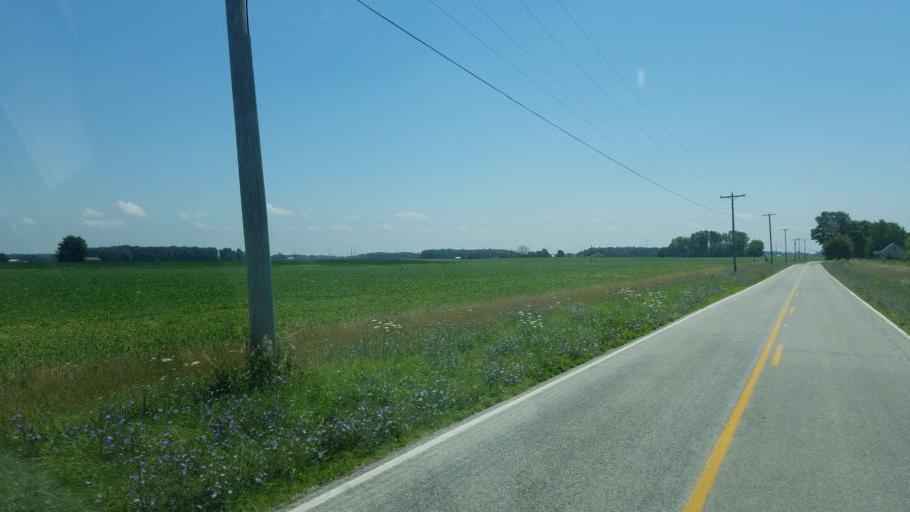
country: US
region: Ohio
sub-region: Sandusky County
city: Fremont
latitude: 41.4177
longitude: -83.0638
